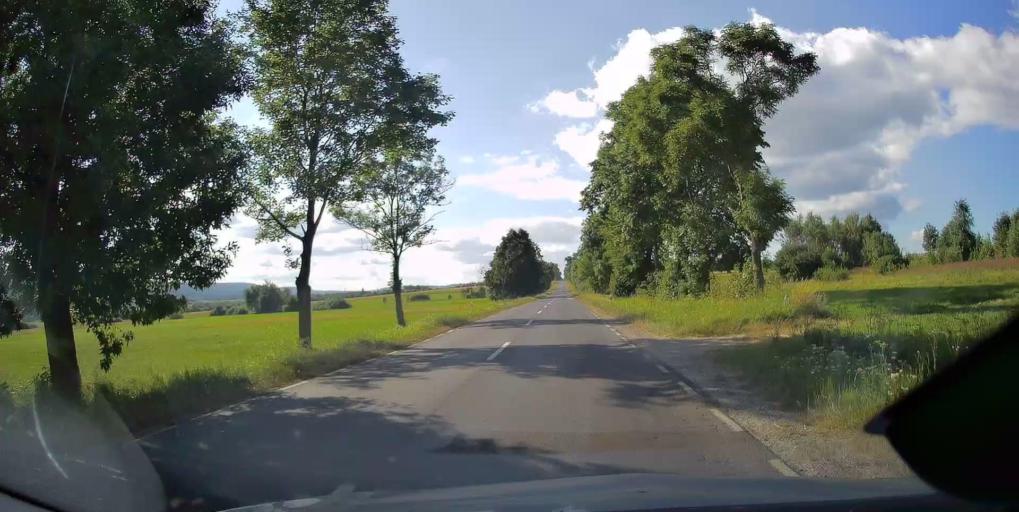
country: PL
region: Swietokrzyskie
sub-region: Powiat kielecki
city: Bodzentyn
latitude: 50.9528
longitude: 20.9223
